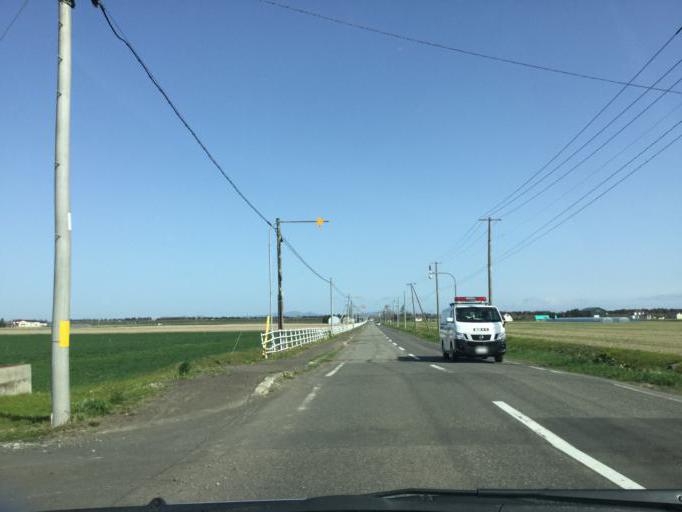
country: JP
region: Hokkaido
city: Iwamizawa
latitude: 43.1467
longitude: 141.7199
